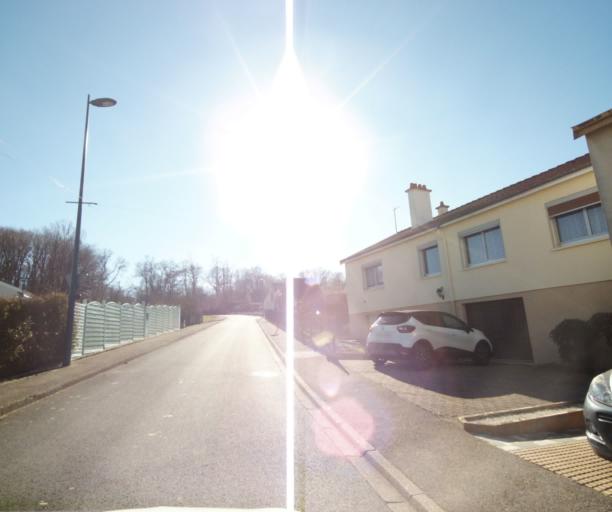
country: FR
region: Lorraine
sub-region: Departement de Meurthe-et-Moselle
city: Saulxures-les-Nancy
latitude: 48.6766
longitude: 6.2421
